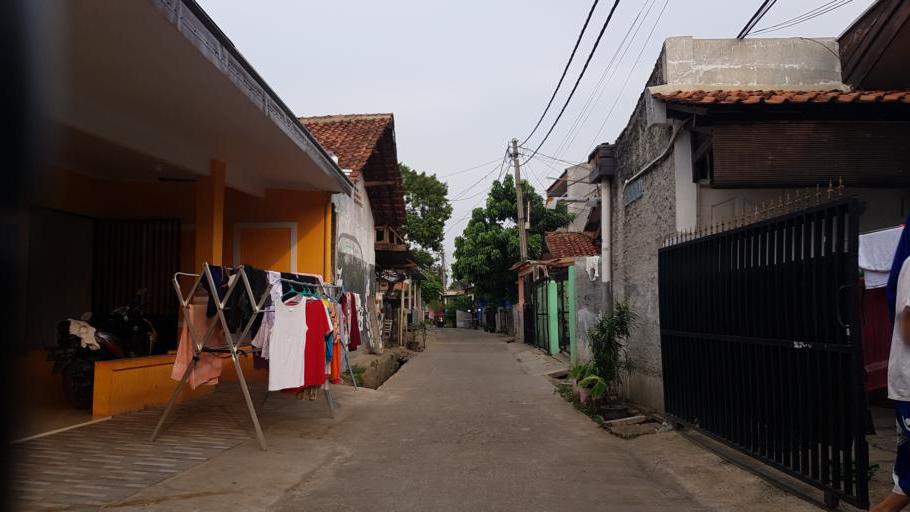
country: ID
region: West Java
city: Depok
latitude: -6.3925
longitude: 106.8001
